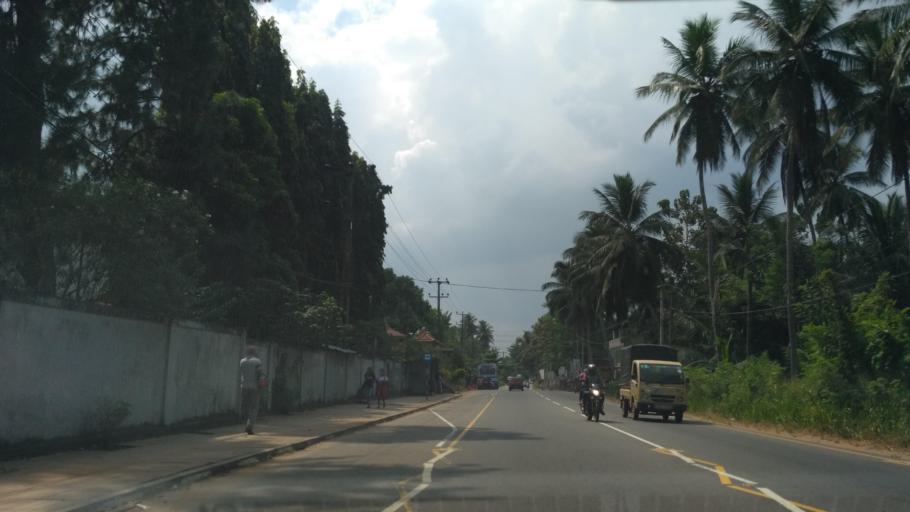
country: LK
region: North Western
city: Kuliyapitiya
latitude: 7.3272
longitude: 80.1184
